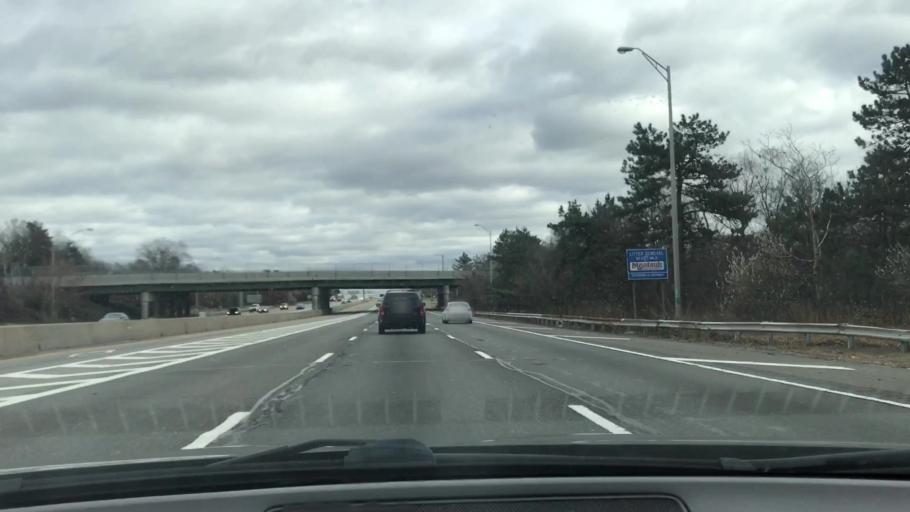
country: US
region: New York
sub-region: Suffolk County
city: Holbrook
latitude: 40.8159
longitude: -73.0869
